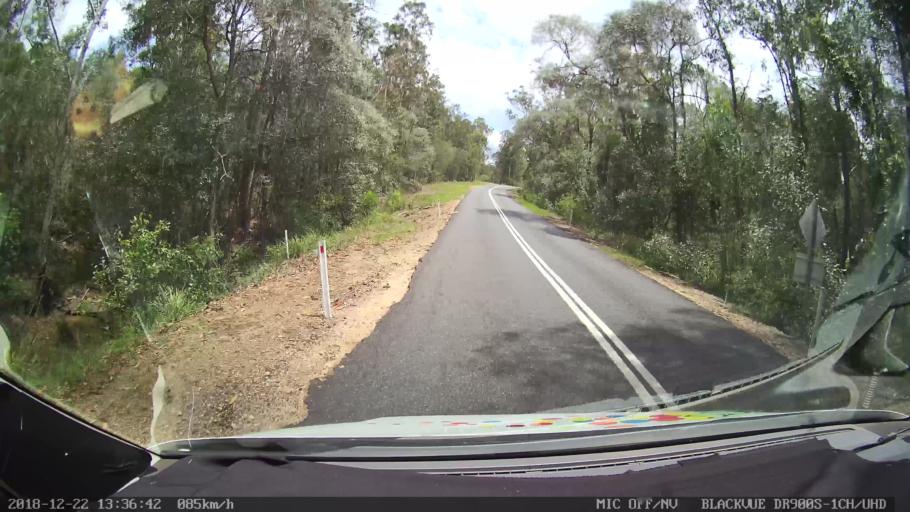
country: AU
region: New South Wales
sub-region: Clarence Valley
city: Coutts Crossing
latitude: -29.8824
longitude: 152.7927
